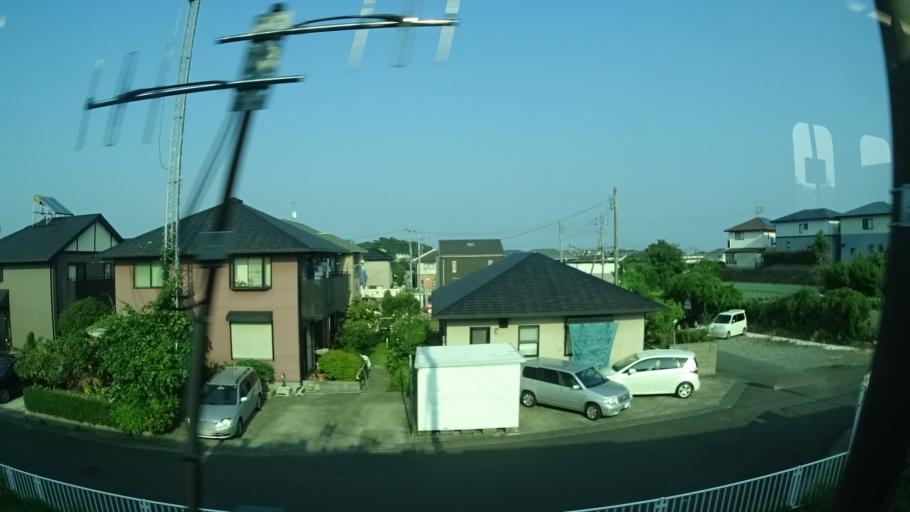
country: JP
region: Ibaraki
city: Hitachi
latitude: 36.6285
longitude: 140.6766
